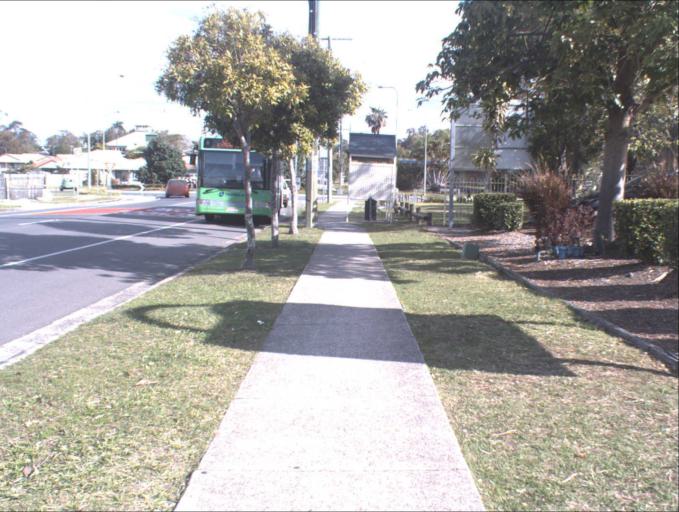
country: AU
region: Queensland
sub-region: Logan
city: Logan Reserve
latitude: -27.6931
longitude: 153.0826
